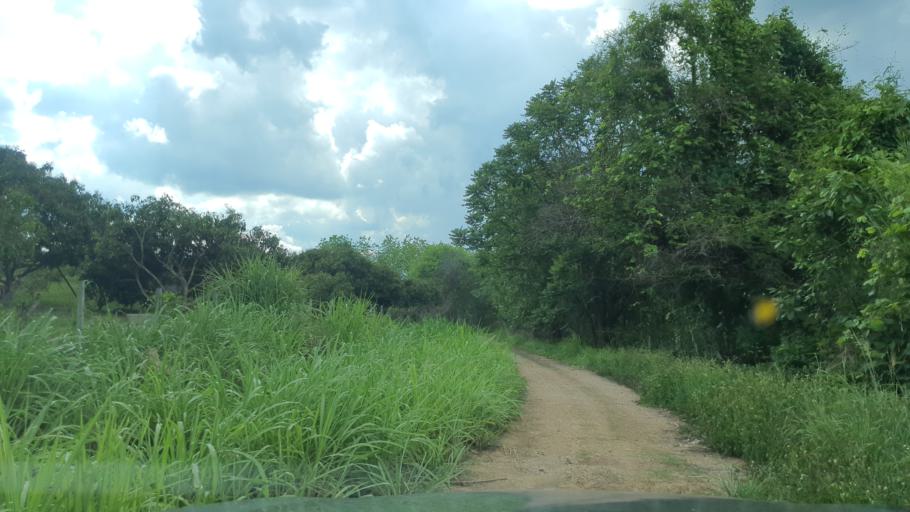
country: TH
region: Chiang Mai
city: Mae Taeng
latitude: 19.1249
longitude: 99.0514
